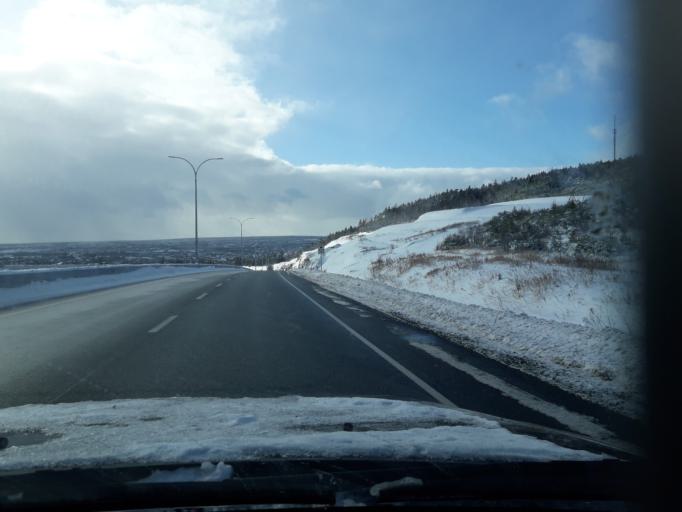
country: CA
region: Newfoundland and Labrador
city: Mount Pearl
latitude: 47.5355
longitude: -52.7767
